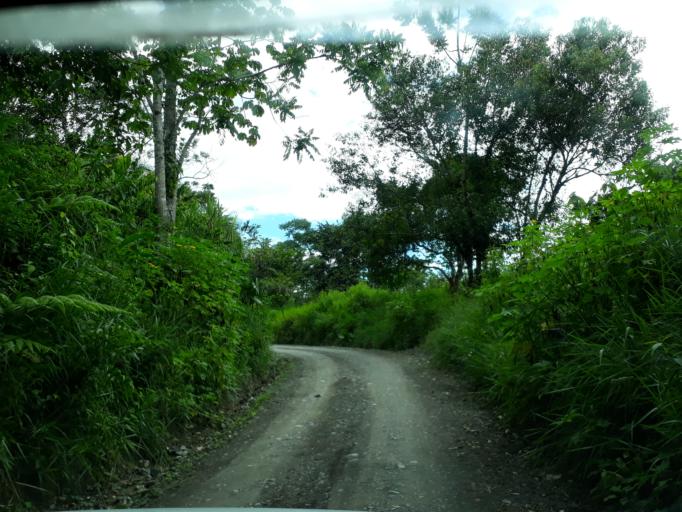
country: CO
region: Boyaca
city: Quipama
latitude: 5.4540
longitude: -74.1748
